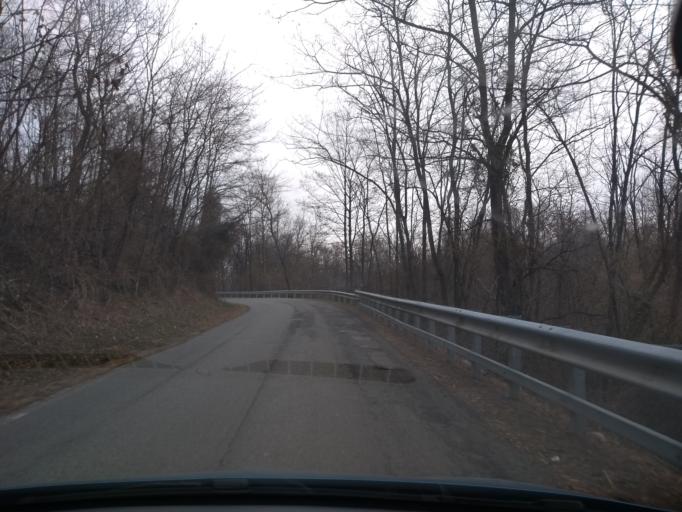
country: IT
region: Piedmont
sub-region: Provincia di Biella
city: Zubiena
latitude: 45.4870
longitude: 7.9881
